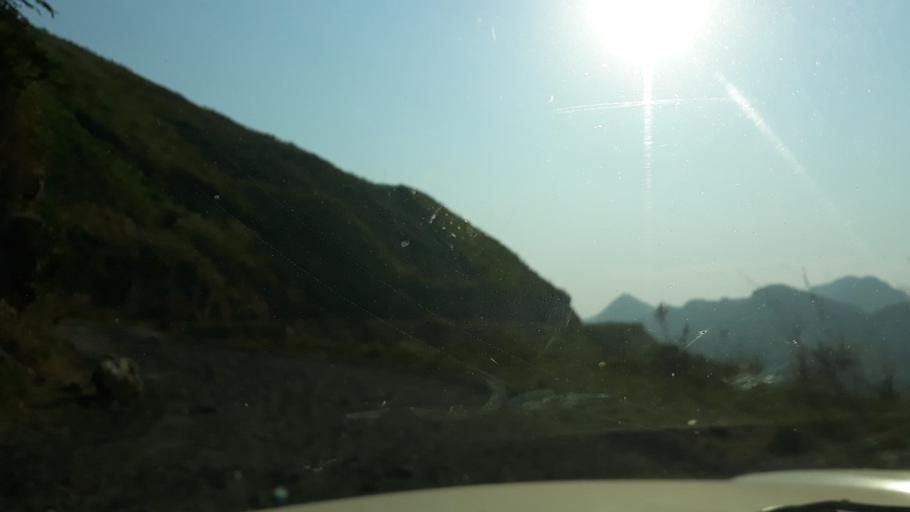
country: BI
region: Cibitoke
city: Cibitoke
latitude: -2.7026
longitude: 28.9855
